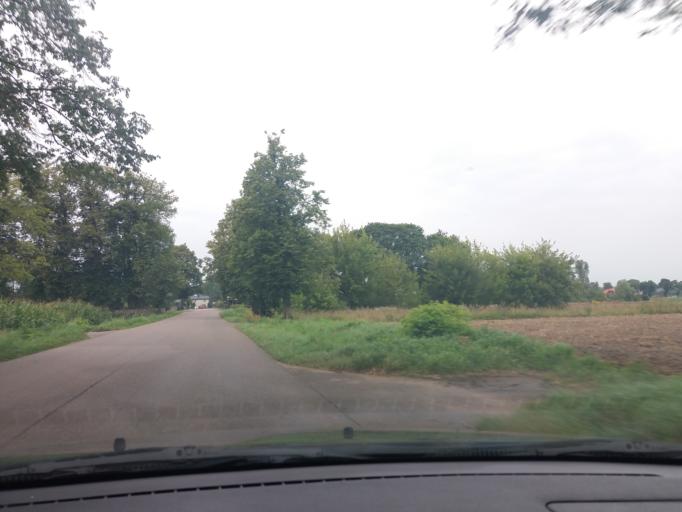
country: PL
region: Masovian Voivodeship
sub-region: Powiat mlawski
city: Wieczfnia Koscielna
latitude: 53.1890
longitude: 20.4440
